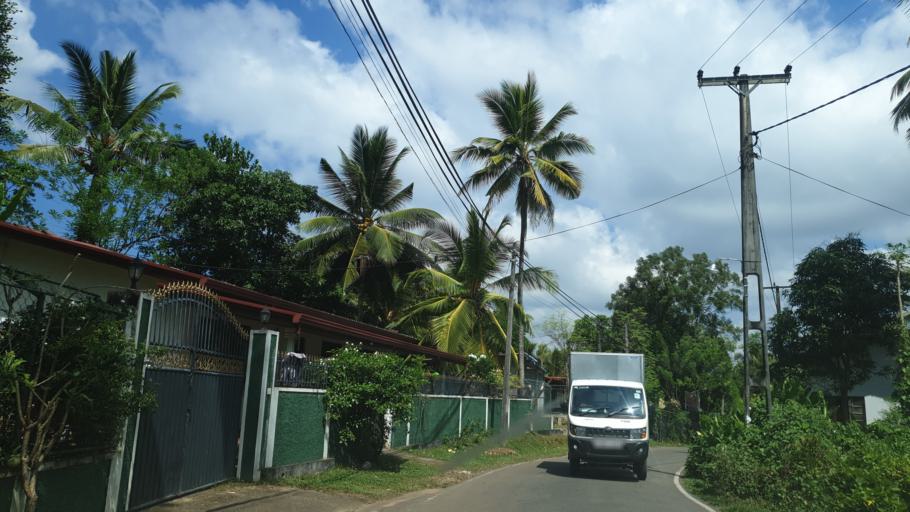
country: LK
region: Western
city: Panadura
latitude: 6.6765
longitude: 79.9392
